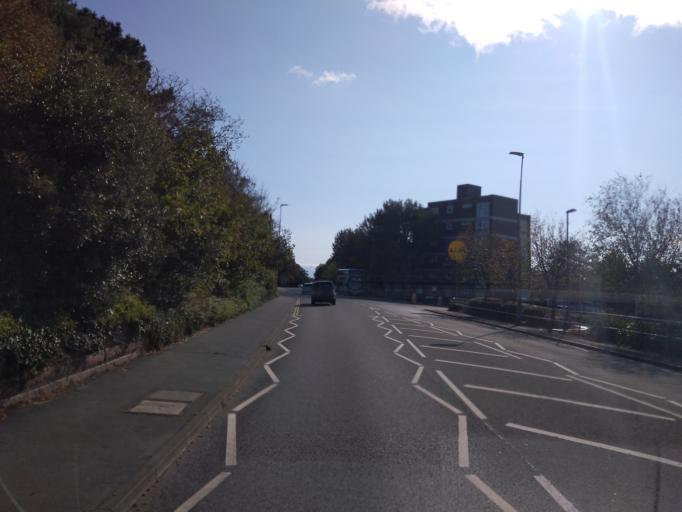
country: GB
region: England
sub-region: East Sussex
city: Hastings
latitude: 50.8601
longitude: 0.5629
